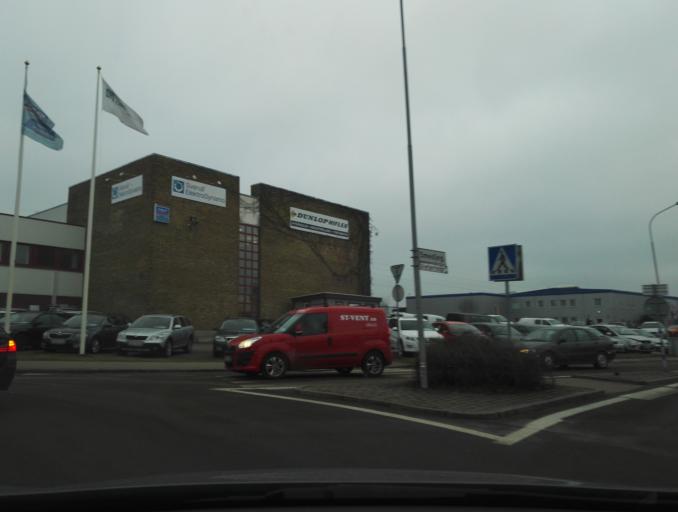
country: SE
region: Kronoberg
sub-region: Vaxjo Kommun
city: Vaexjoe
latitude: 56.8879
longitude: 14.7791
